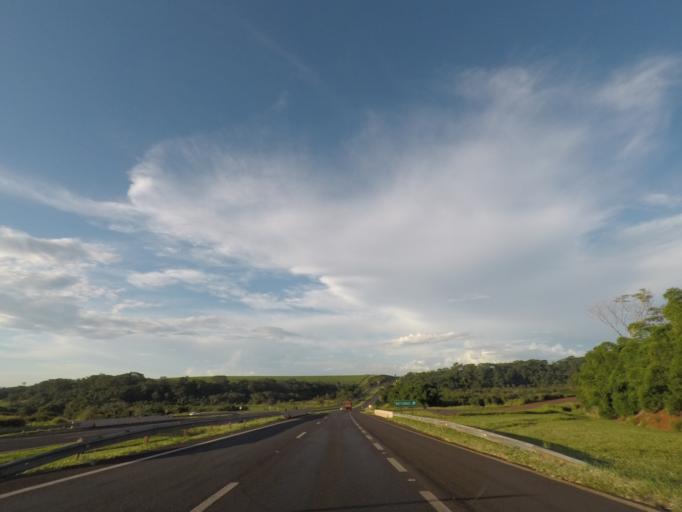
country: BR
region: Sao Paulo
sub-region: Ituverava
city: Ituverava
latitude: -20.2613
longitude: -47.7998
